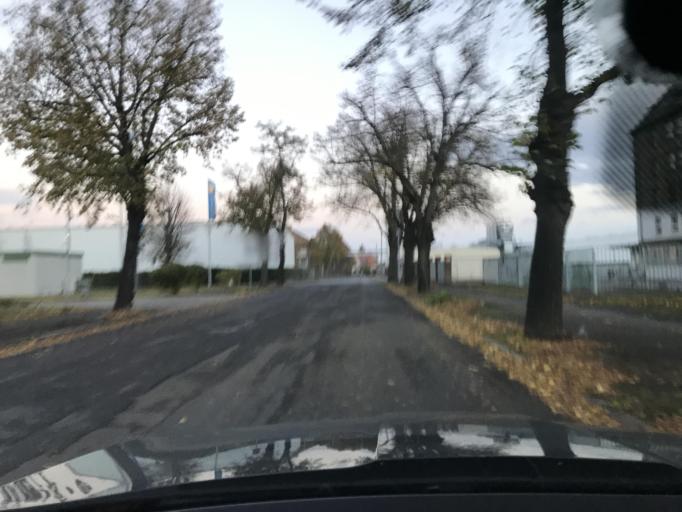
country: DE
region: Saxony-Anhalt
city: Halberstadt
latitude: 51.8868
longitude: 11.0604
